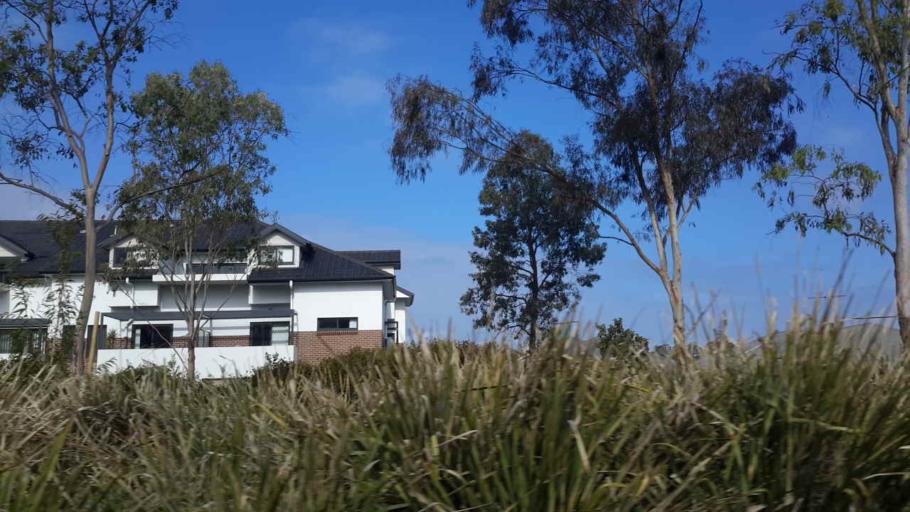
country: AU
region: New South Wales
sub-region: Campbelltown Municipality
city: Glen Alpine
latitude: -34.0759
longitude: 150.8001
